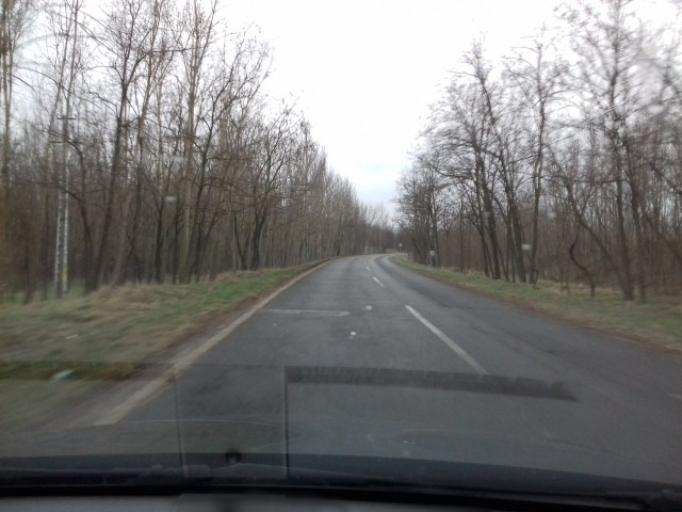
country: HU
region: Szabolcs-Szatmar-Bereg
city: Nyirbogdany
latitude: 48.0802
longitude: 21.8621
